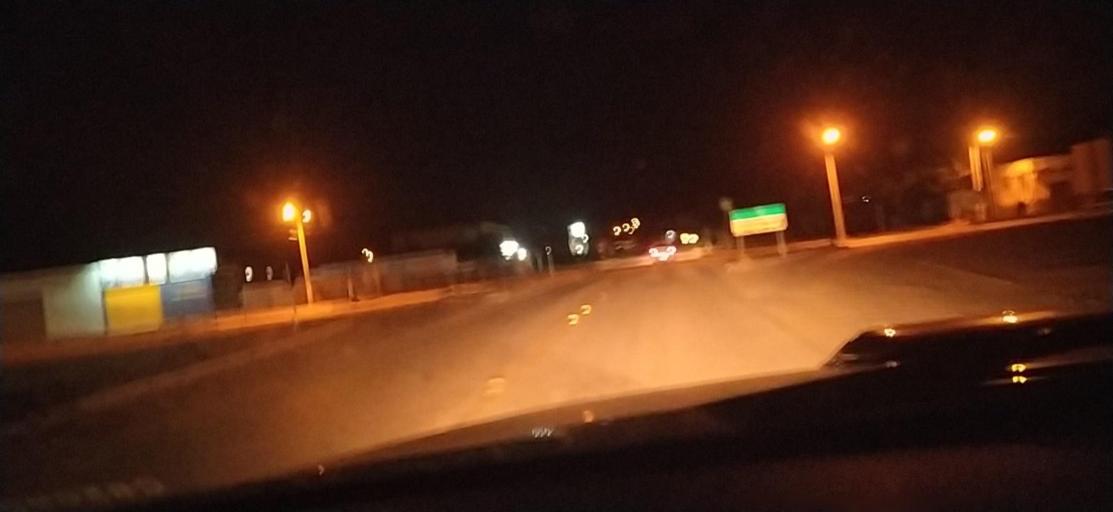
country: BR
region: Minas Gerais
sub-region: Monte Azul
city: Monte Azul
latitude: -15.1525
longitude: -42.8623
